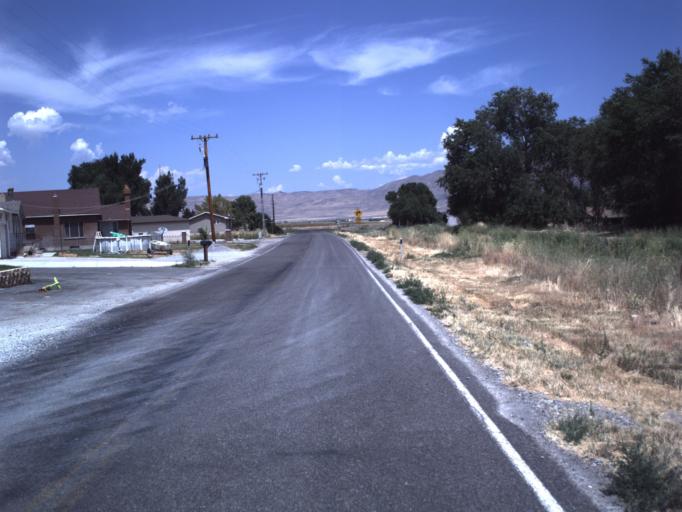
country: US
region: Utah
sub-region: Box Elder County
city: Tremonton
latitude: 41.6915
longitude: -112.2956
